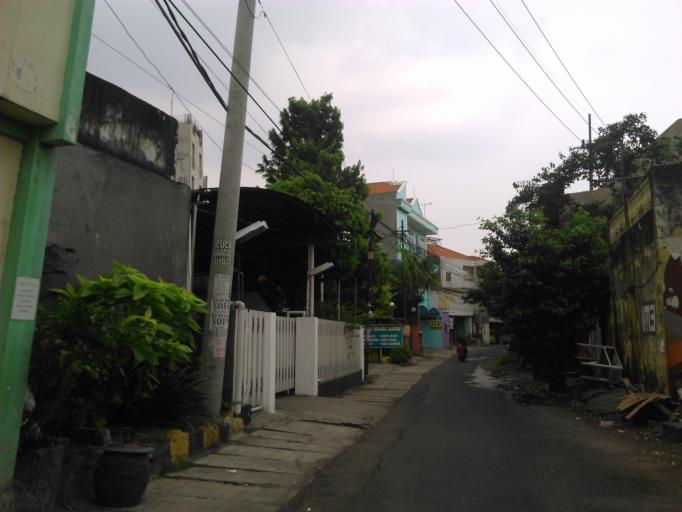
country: ID
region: East Java
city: Gubengairlangga
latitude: -7.2715
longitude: 112.7607
